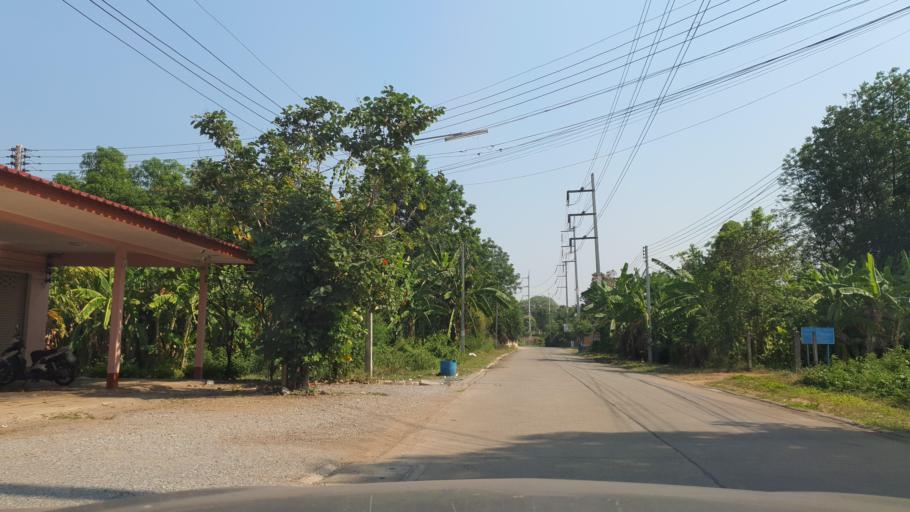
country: TH
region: Kanchanaburi
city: Kanchanaburi
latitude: 14.0662
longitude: 99.4858
